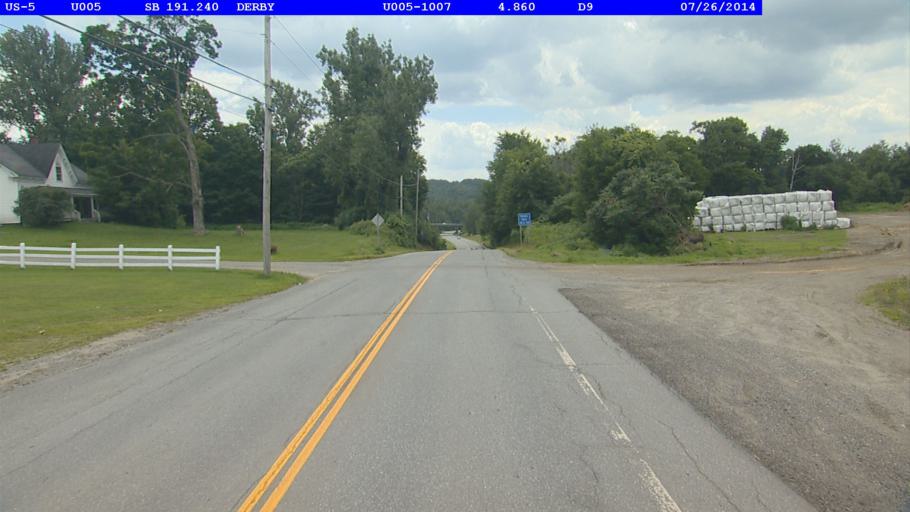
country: US
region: Vermont
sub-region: Orleans County
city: Newport
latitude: 44.9914
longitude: -72.1065
